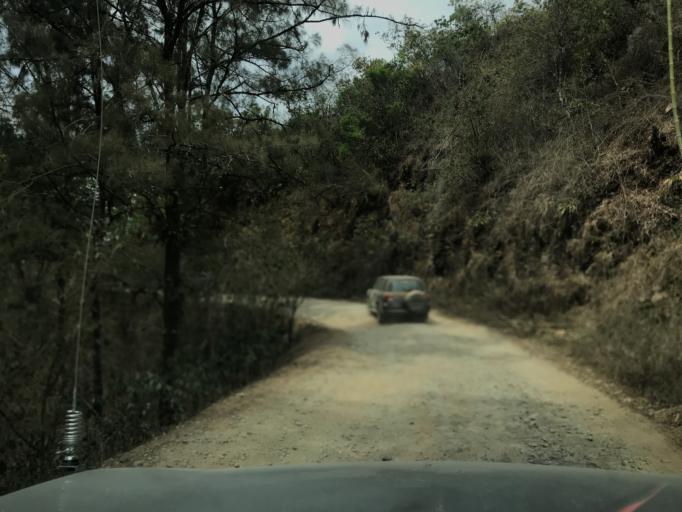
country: TL
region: Ermera
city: Gleno
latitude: -8.8226
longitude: 125.4334
